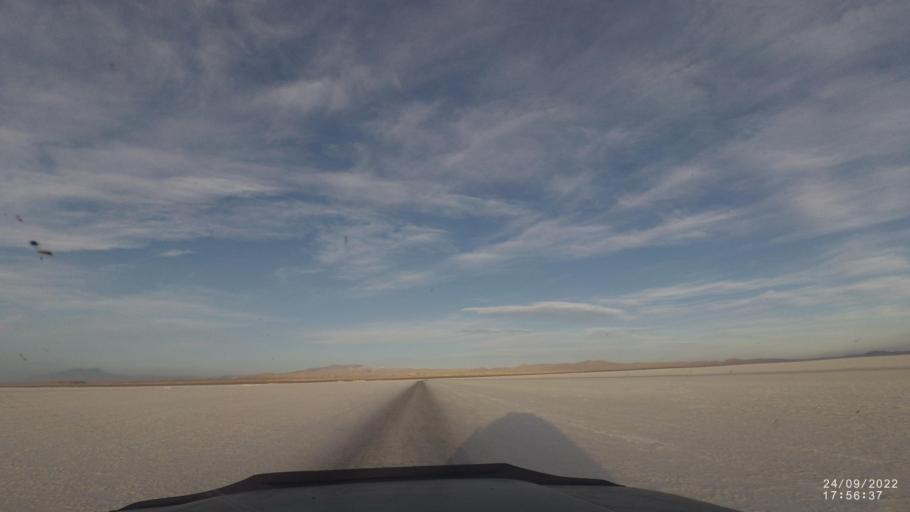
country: BO
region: Potosi
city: Colchani
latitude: -20.3237
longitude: -67.0089
